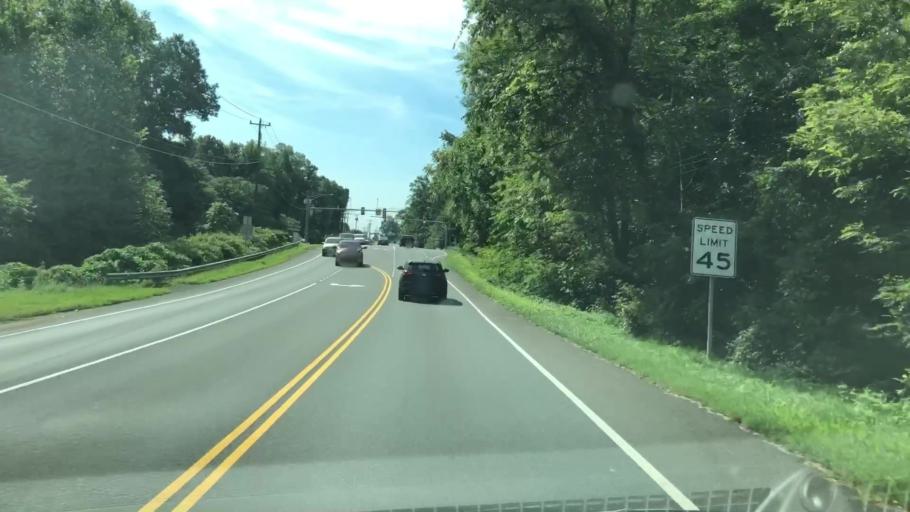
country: US
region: Virginia
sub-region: City of Fredericksburg
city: Fredericksburg
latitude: 38.2759
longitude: -77.4513
